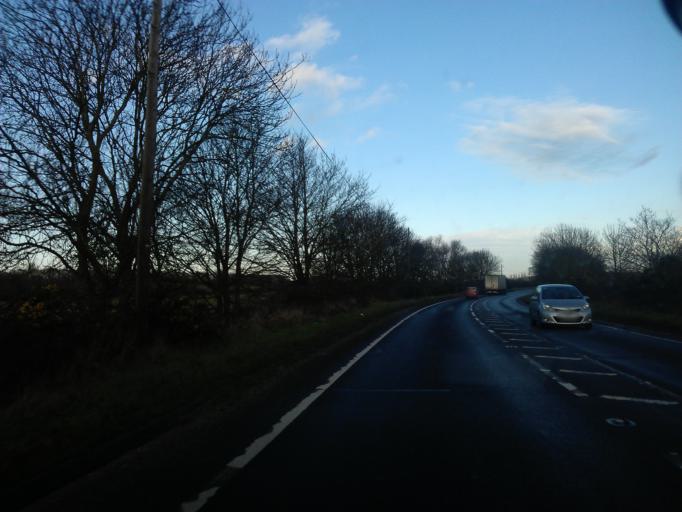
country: GB
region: England
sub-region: Suffolk
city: Shotley Gate
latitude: 51.9336
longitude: 1.2261
